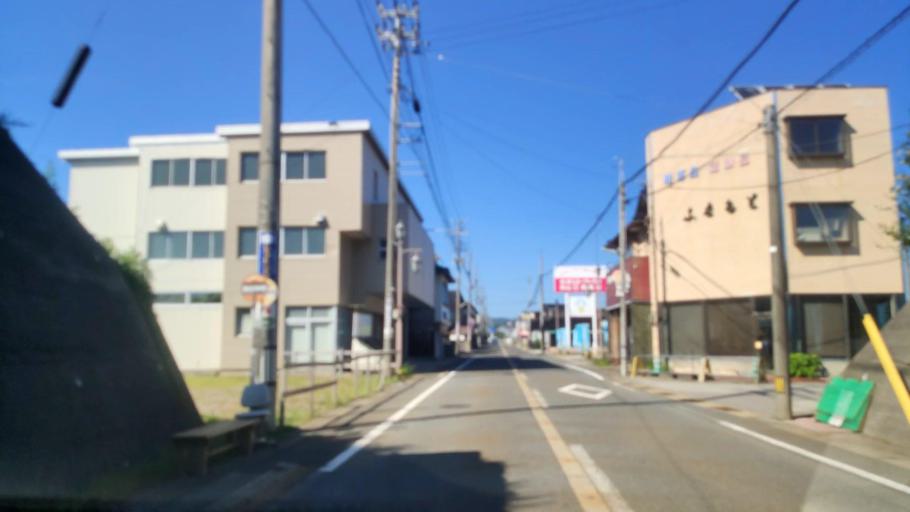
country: JP
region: Ishikawa
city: Nanao
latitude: 37.4405
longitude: 137.2650
